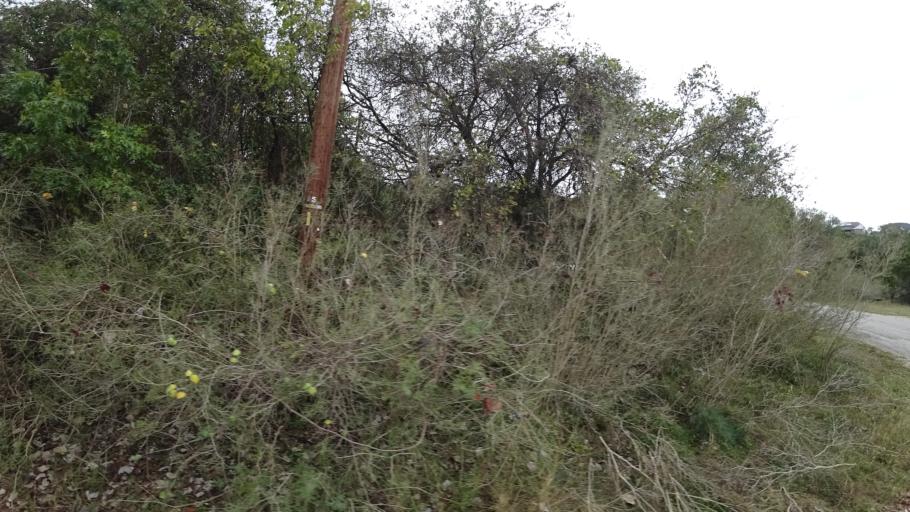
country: US
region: Texas
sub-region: Travis County
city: Bee Cave
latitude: 30.3381
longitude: -97.9048
